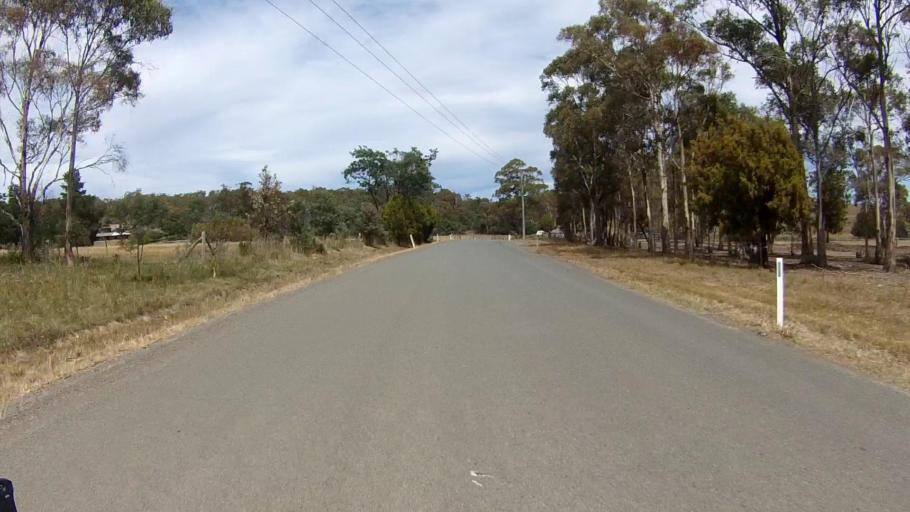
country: AU
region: Tasmania
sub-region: Sorell
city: Sorell
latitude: -42.8033
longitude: 147.6444
